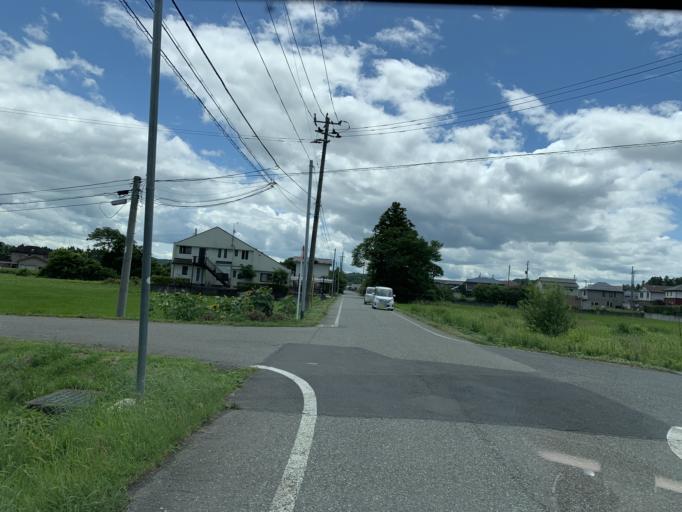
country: JP
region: Iwate
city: Ichinoseki
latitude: 38.9348
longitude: 141.0945
